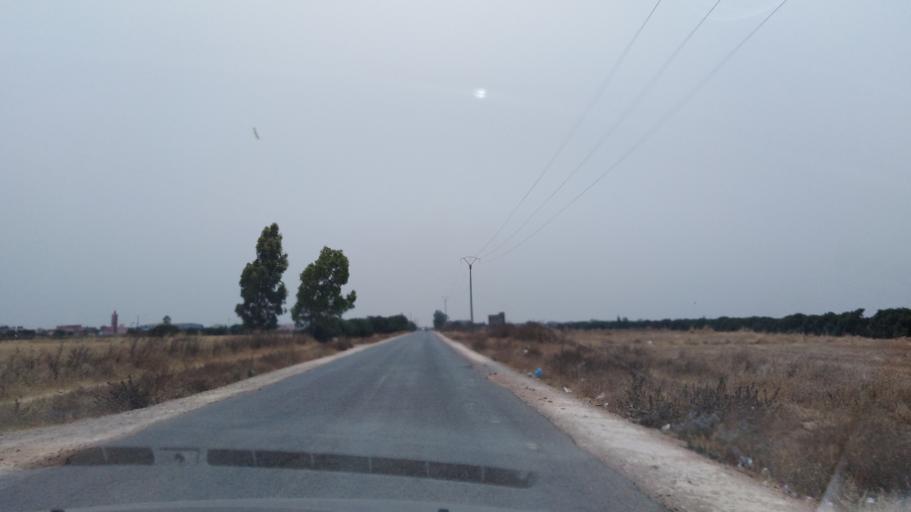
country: MA
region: Grand Casablanca
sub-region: Mediouna
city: Mediouna
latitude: 33.4208
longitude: -7.5219
